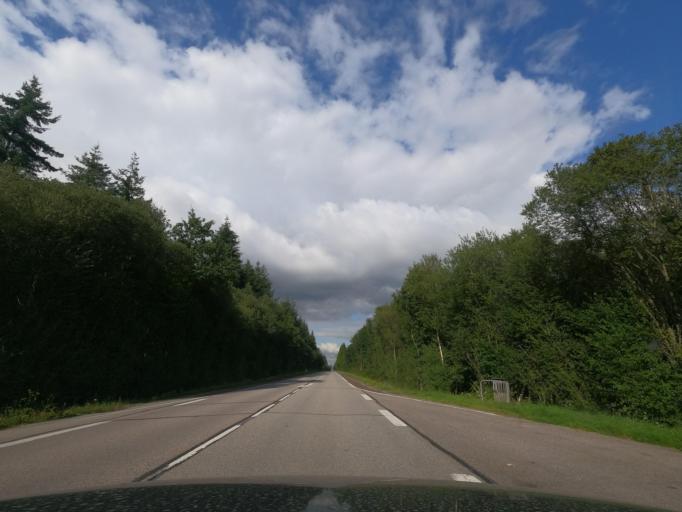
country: FR
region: Lower Normandy
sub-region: Departement de l'Orne
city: Gace
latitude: 48.8357
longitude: 0.3410
